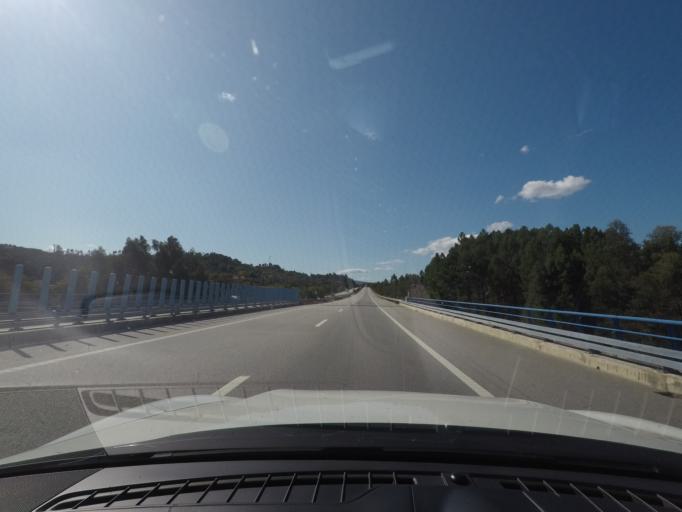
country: PT
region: Vila Real
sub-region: Mondim de Basto
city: Mondim de Basto
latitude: 41.4793
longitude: -7.9047
